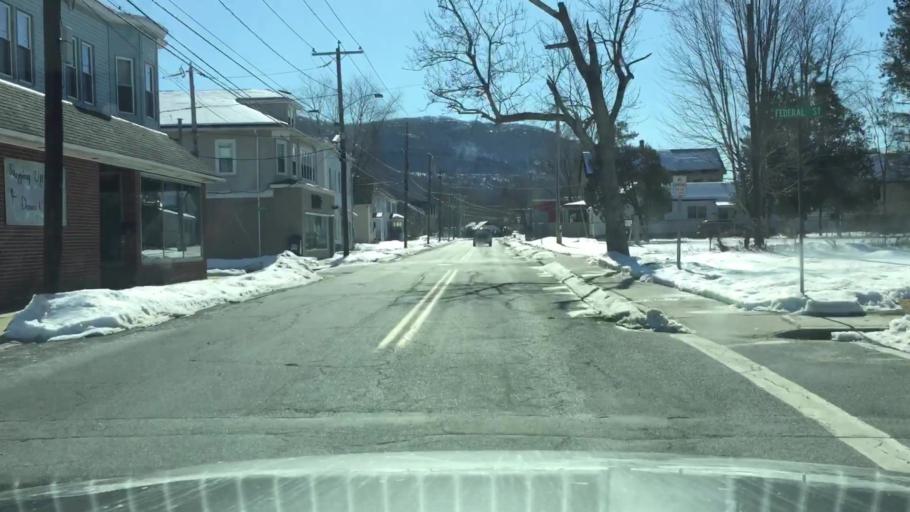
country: US
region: Massachusetts
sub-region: Hampshire County
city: Easthampton
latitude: 42.2739
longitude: -72.6521
